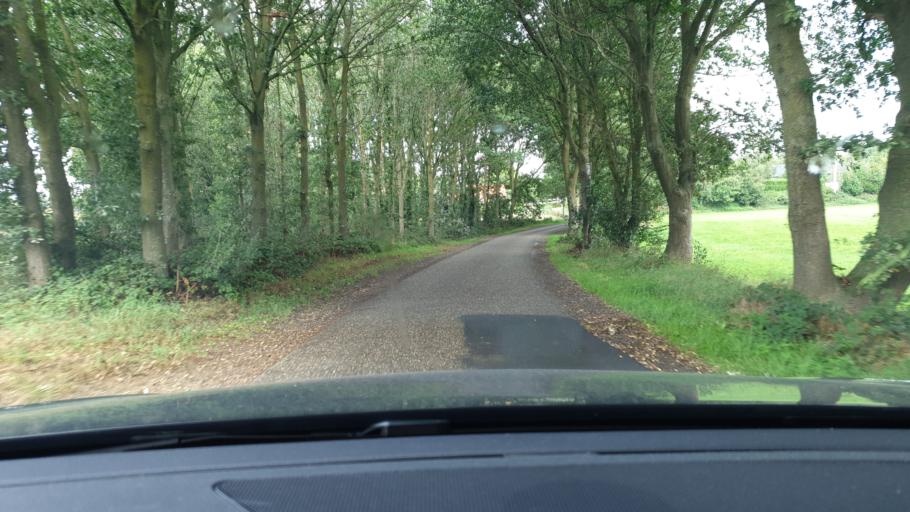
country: NL
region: Limburg
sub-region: Gemeente Venray
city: Venray
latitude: 51.5463
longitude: 6.0528
